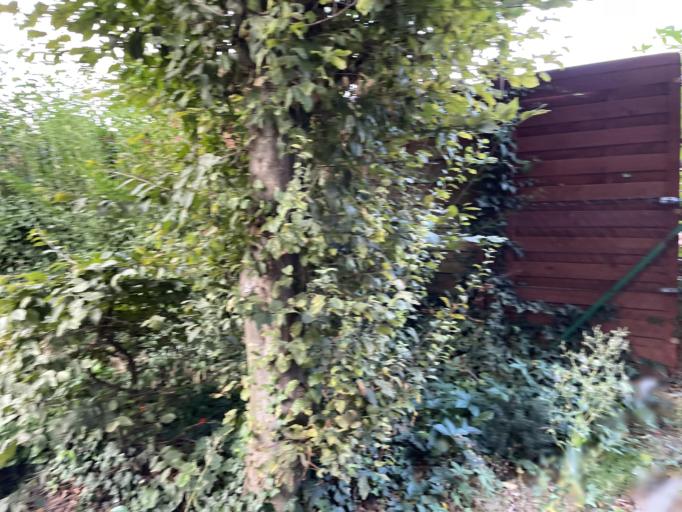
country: DE
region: North Rhine-Westphalia
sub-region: Regierungsbezirk Koln
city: Bergheim
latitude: 50.9463
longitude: 6.6456
